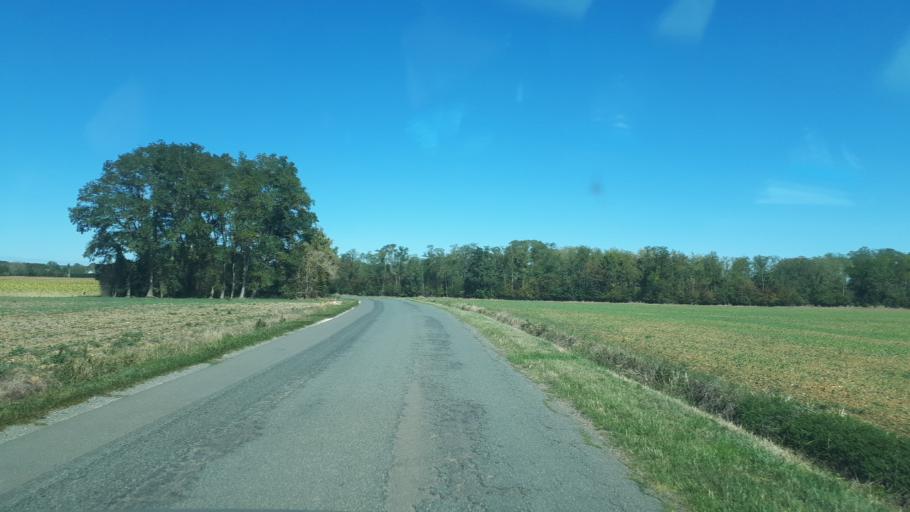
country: FR
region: Centre
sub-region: Departement du Cher
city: Rians
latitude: 47.1888
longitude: 2.7136
